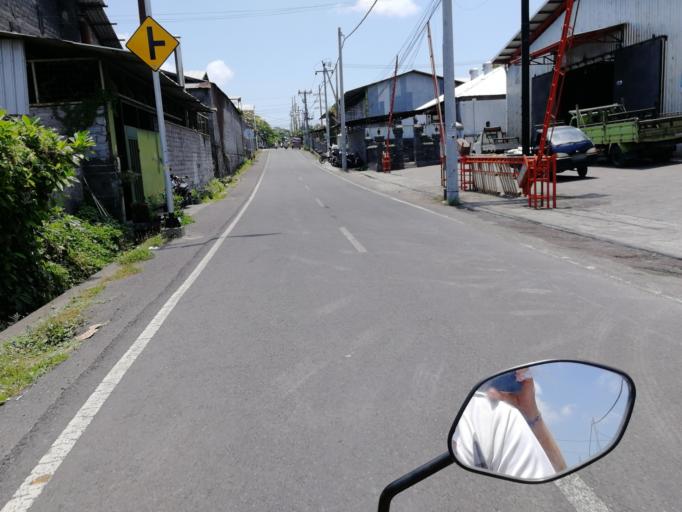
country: ID
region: Bali
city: Banjar Kertasari
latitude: -8.6378
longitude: 115.1772
